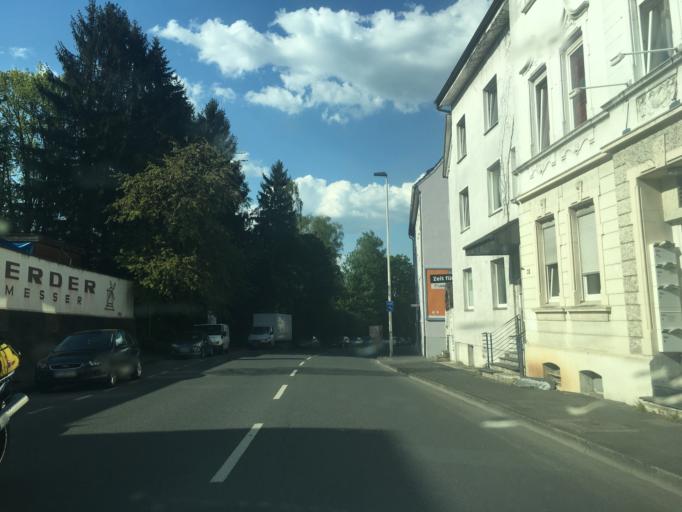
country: DE
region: North Rhine-Westphalia
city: Haan
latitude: 51.1650
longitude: 6.9956
